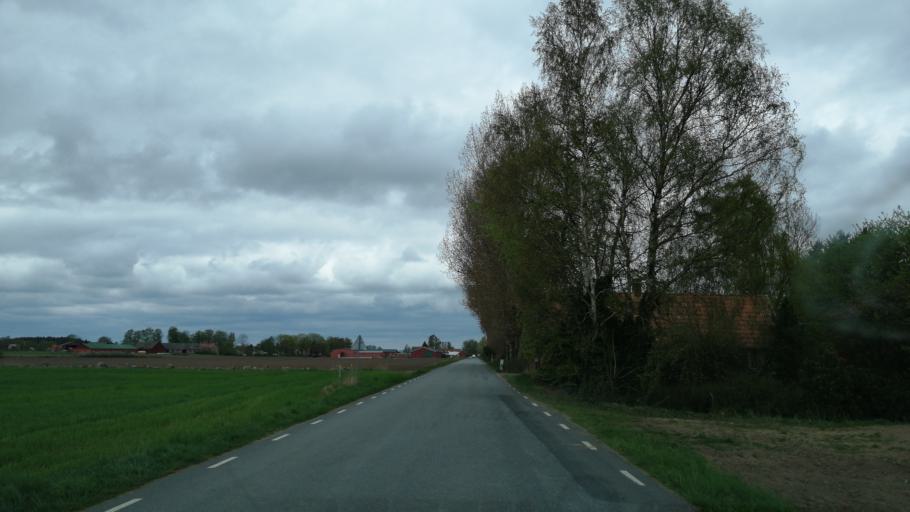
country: SE
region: Skane
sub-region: Kristianstads Kommun
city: Fjalkinge
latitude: 56.0591
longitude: 14.3326
